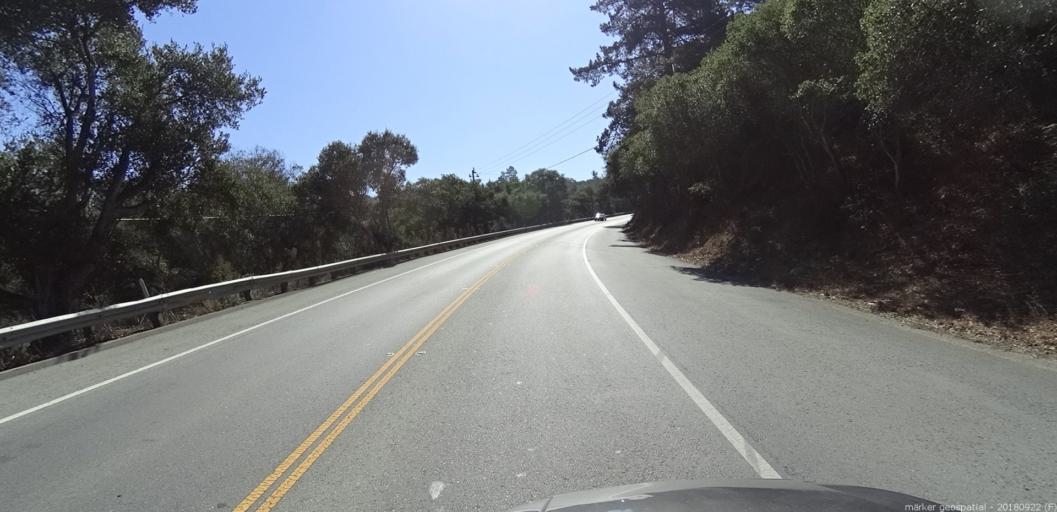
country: US
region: California
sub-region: Monterey County
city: Prunedale
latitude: 36.8347
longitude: -121.6809
